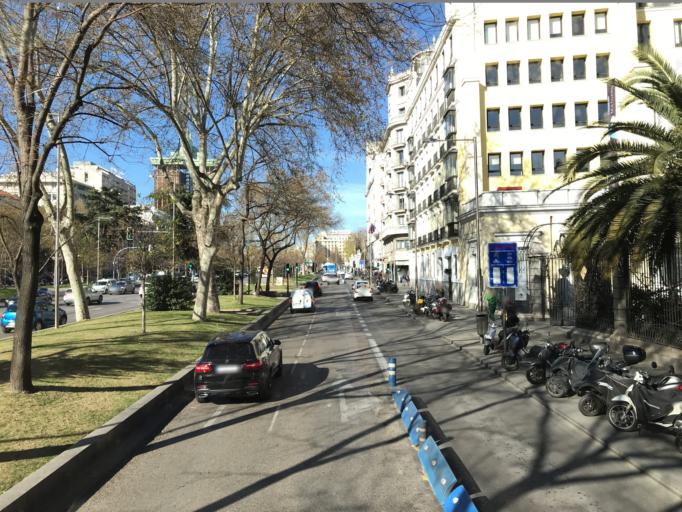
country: ES
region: Madrid
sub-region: Provincia de Madrid
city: City Center
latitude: 40.4216
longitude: -3.6916
